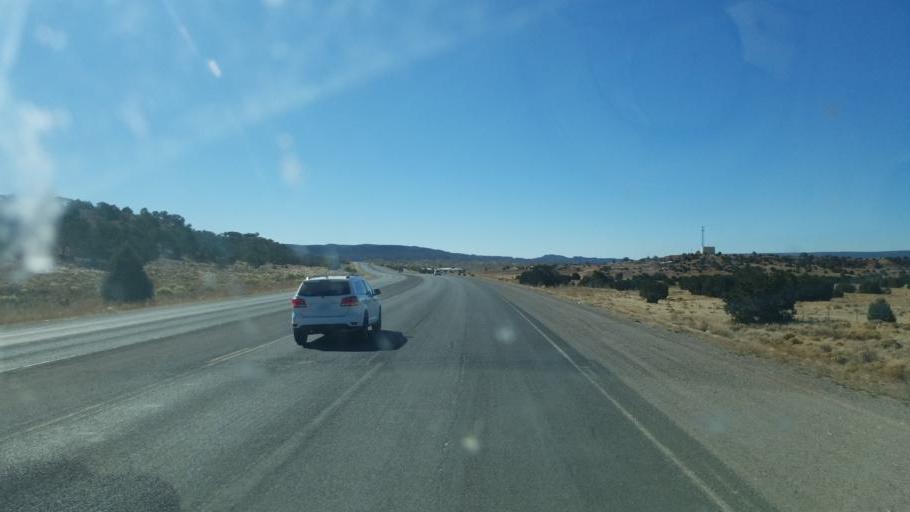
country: US
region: Arizona
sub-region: Apache County
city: Window Rock
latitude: 35.6908
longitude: -109.0649
